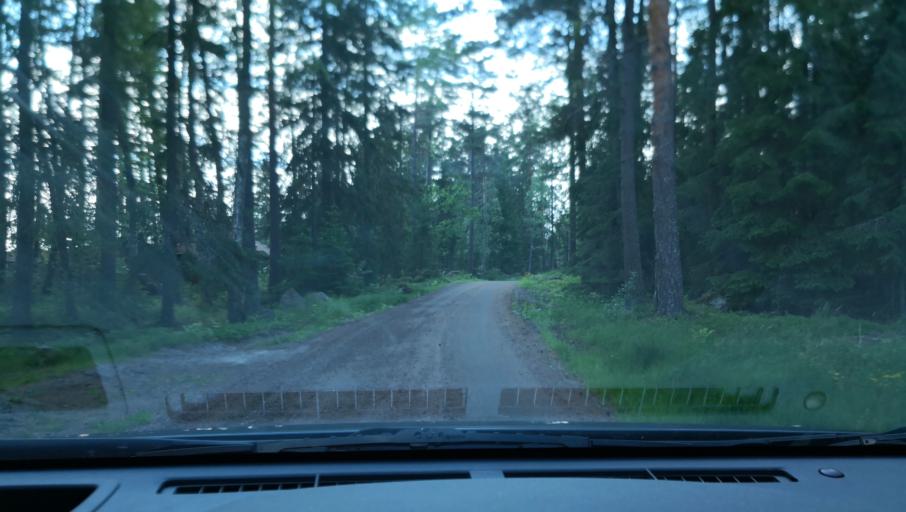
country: SE
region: Uppsala
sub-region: Enkopings Kommun
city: Orsundsbro
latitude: 59.8365
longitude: 17.2255
